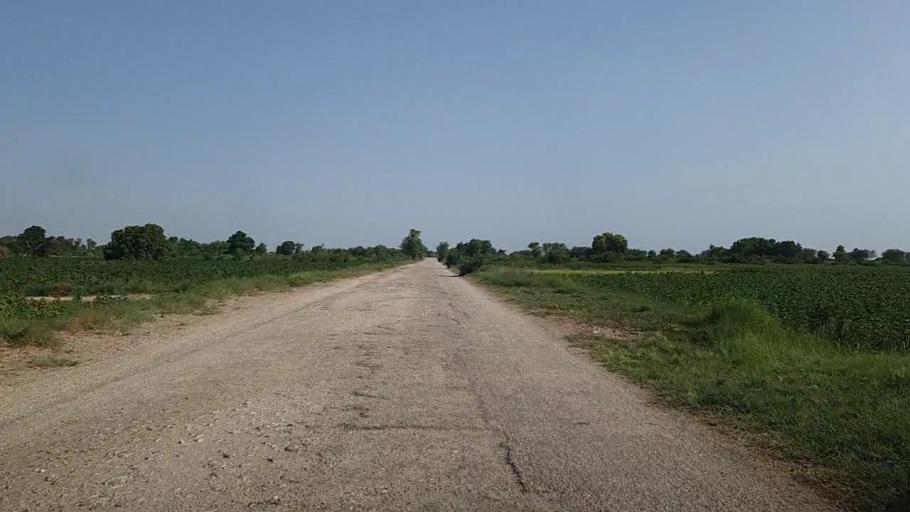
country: PK
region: Sindh
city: Karaundi
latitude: 26.8734
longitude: 68.3284
